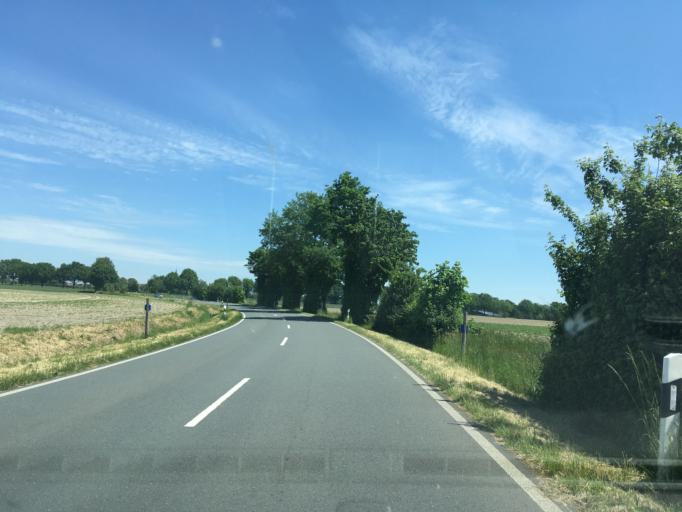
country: DE
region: North Rhine-Westphalia
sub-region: Regierungsbezirk Munster
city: Sudlohn
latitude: 51.8997
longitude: 6.8411
